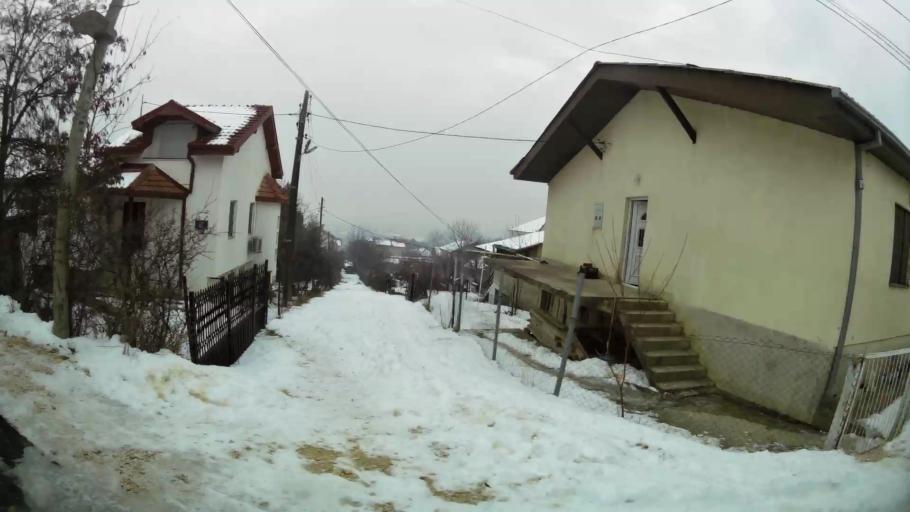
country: MK
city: Kondovo
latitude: 42.0379
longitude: 21.3439
